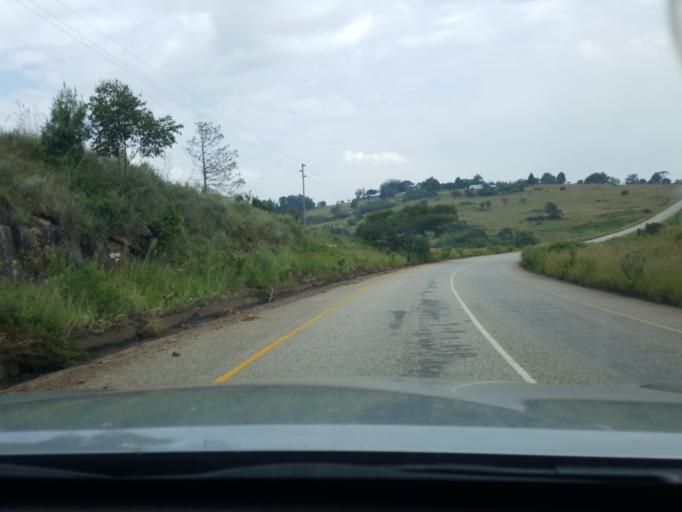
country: ZA
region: Mpumalanga
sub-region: Ehlanzeni District
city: White River
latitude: -25.1997
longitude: 30.9392
